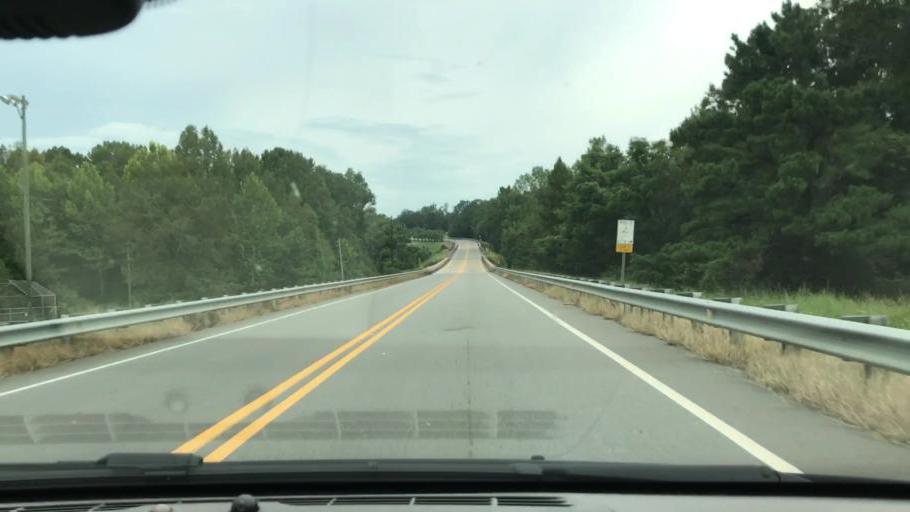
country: US
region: Alabama
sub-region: Houston County
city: Ashford
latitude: 31.2881
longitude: -85.1025
